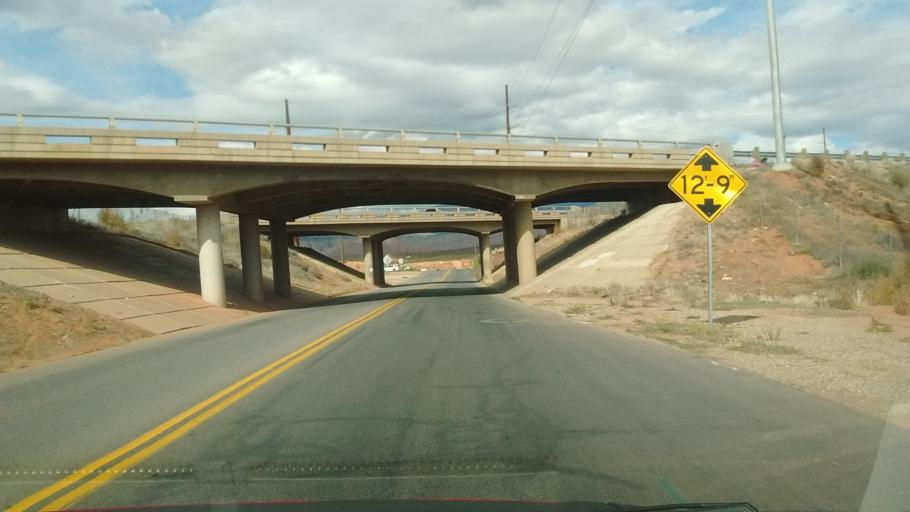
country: US
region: Utah
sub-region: Washington County
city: Washington
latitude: 37.1383
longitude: -113.5098
